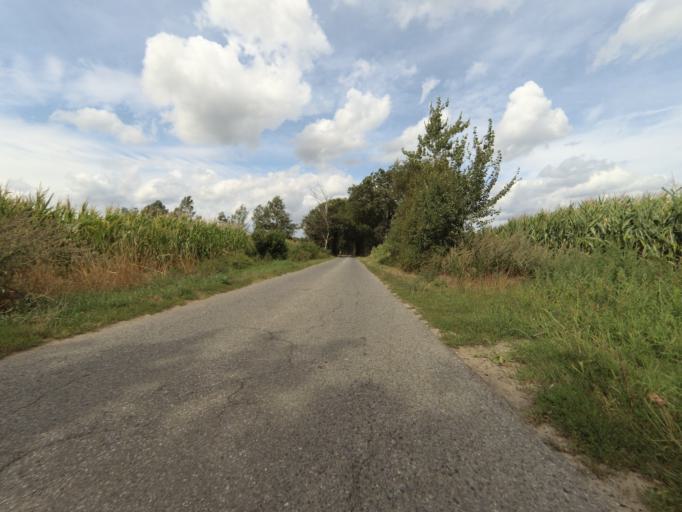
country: DE
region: North Rhine-Westphalia
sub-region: Regierungsbezirk Munster
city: Ahaus
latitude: 52.1419
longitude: 6.9945
